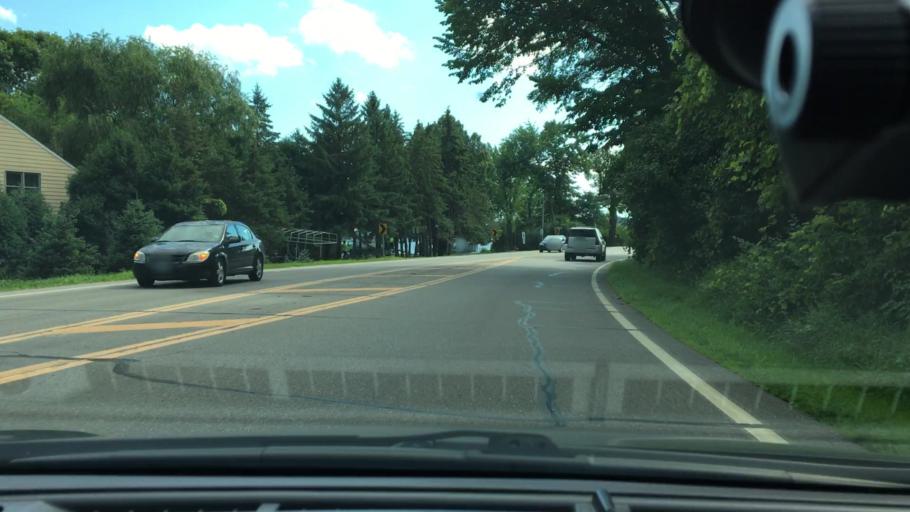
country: US
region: Minnesota
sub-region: Hennepin County
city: Tonka Bay
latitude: 44.9391
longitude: -93.5826
